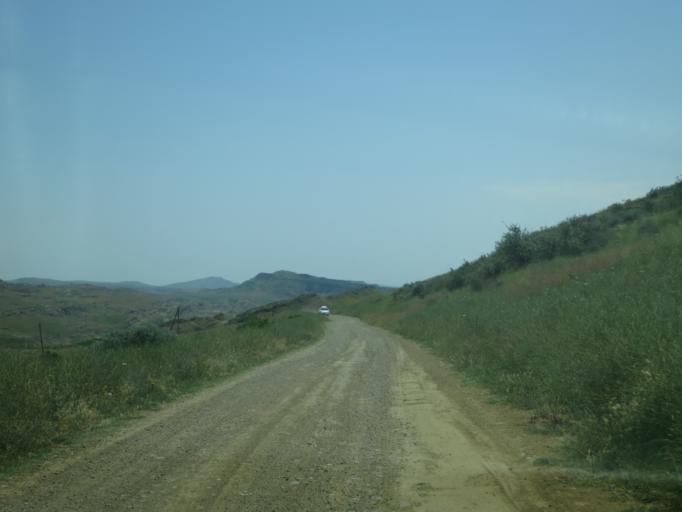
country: AZ
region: Agstafa
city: Saloglu
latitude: 41.4541
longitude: 45.3686
